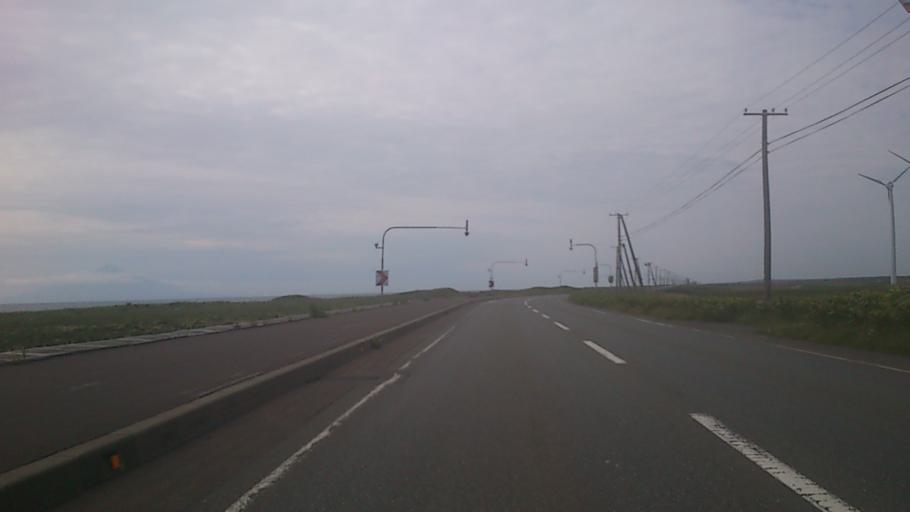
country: JP
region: Hokkaido
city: Makubetsu
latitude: 44.9757
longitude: 141.6962
